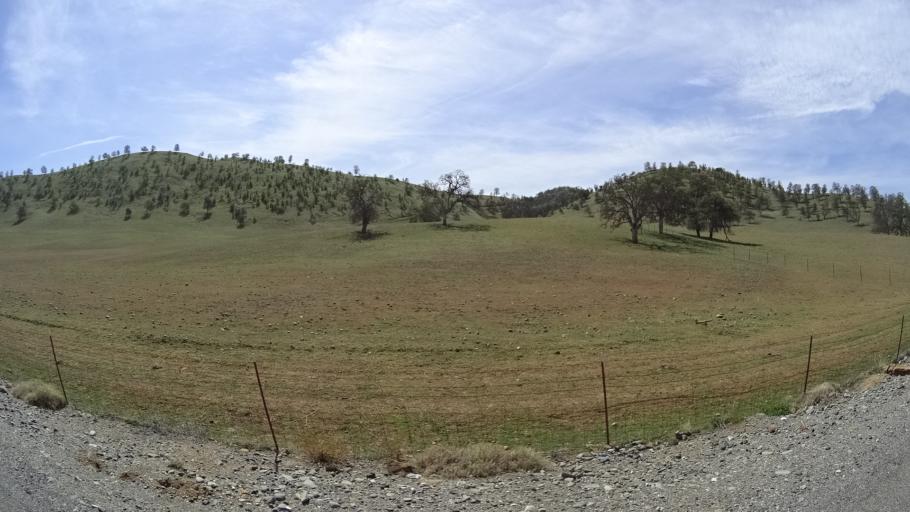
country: US
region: California
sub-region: Glenn County
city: Willows
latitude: 39.5390
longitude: -122.4469
